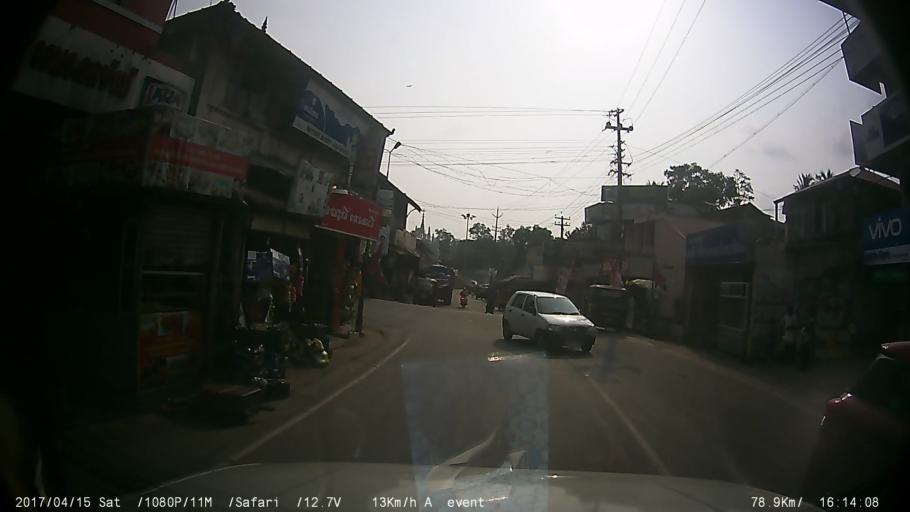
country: IN
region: Kerala
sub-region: Kottayam
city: Kottayam
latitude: 9.6680
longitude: 76.5332
